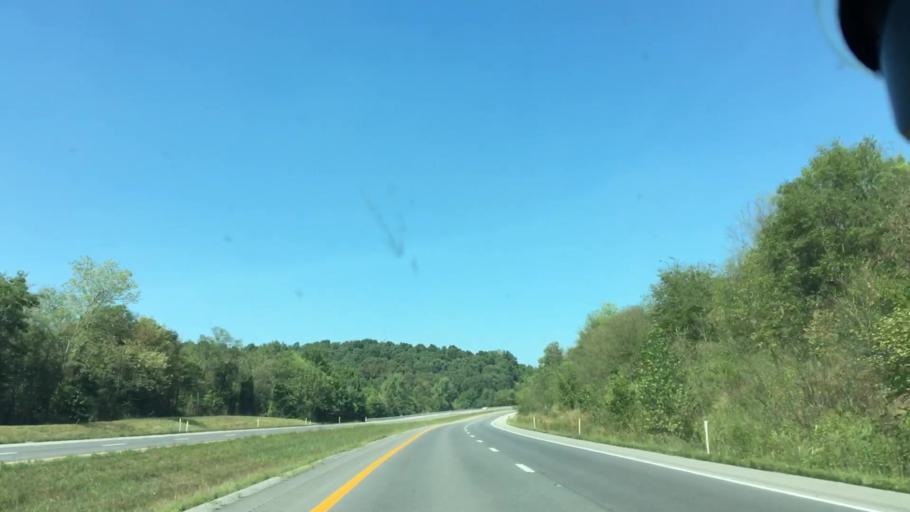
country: US
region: Kentucky
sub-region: Webster County
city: Sebree
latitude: 37.5930
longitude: -87.4935
